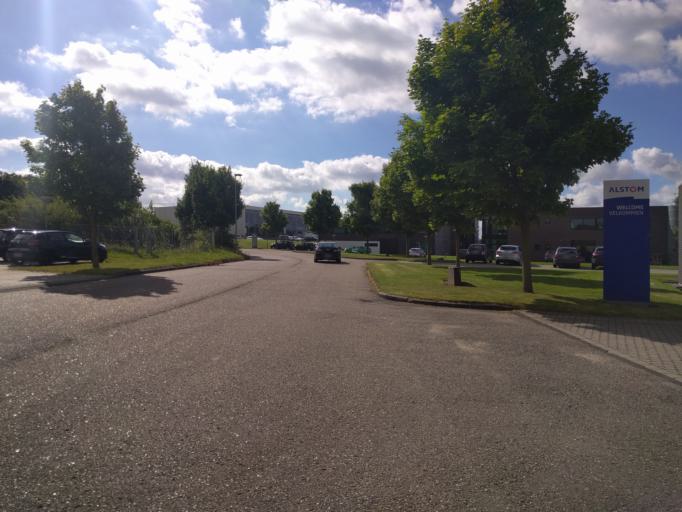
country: DK
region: South Denmark
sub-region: Fredericia Kommune
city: Snoghoj
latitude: 55.5328
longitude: 9.7204
